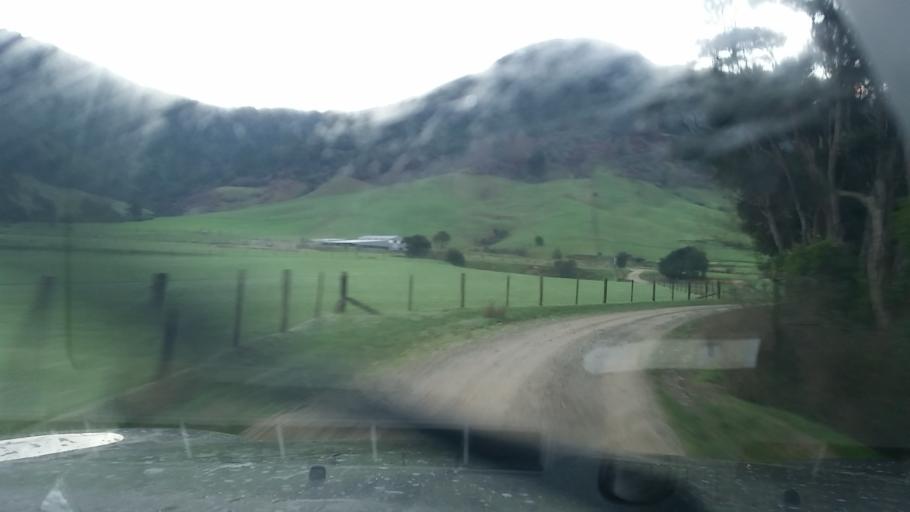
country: NZ
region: Marlborough
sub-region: Marlborough District
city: Picton
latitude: -41.1572
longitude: 174.1315
